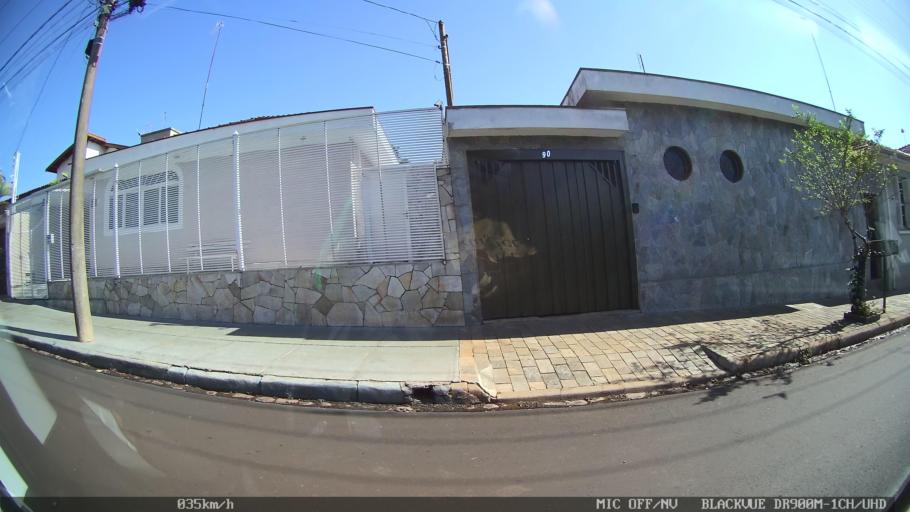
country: BR
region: Sao Paulo
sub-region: Batatais
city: Batatais
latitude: -20.8921
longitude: -47.5799
